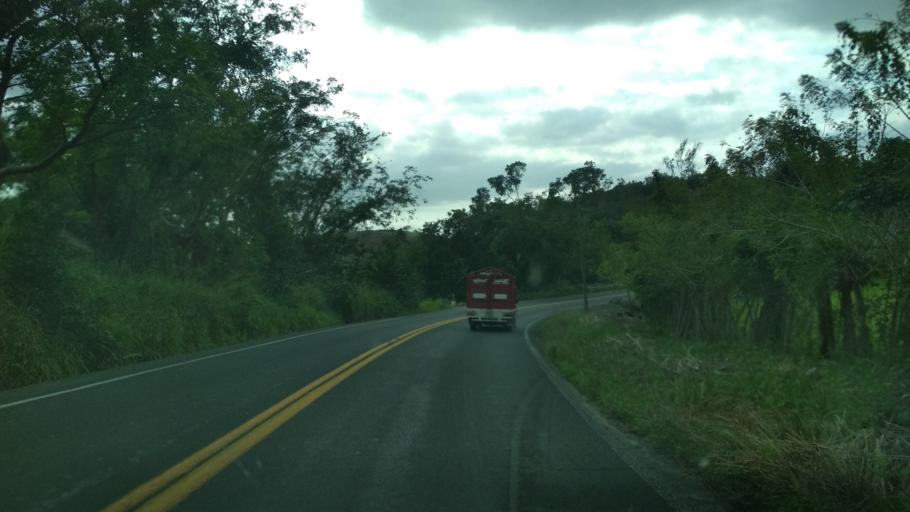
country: MX
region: Veracruz
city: Papantla de Olarte
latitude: 20.4632
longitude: -97.2663
